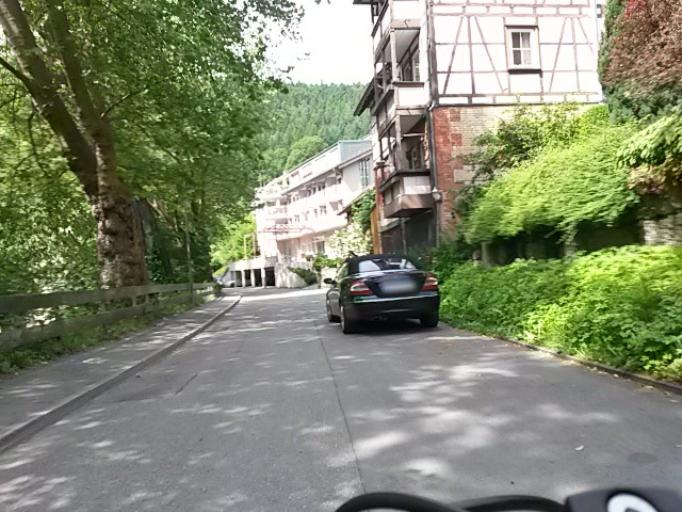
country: DE
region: Baden-Wuerttemberg
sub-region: Karlsruhe Region
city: Calw
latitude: 48.7051
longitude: 8.7339
